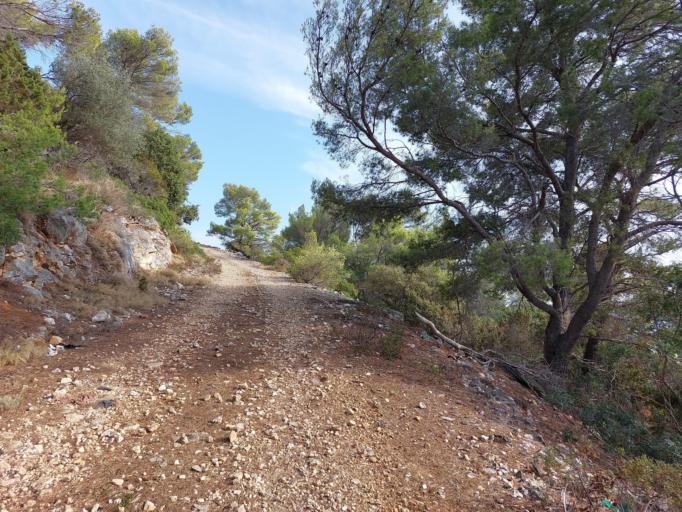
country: HR
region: Dubrovacko-Neretvanska
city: Smokvica
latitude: 42.7334
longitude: 16.8294
